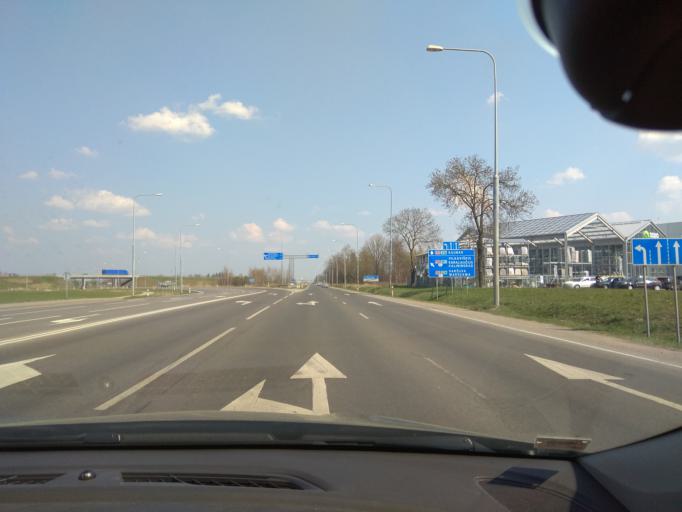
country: LT
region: Marijampoles apskritis
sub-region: Marijampole Municipality
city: Marijampole
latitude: 54.5813
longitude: 23.3768
